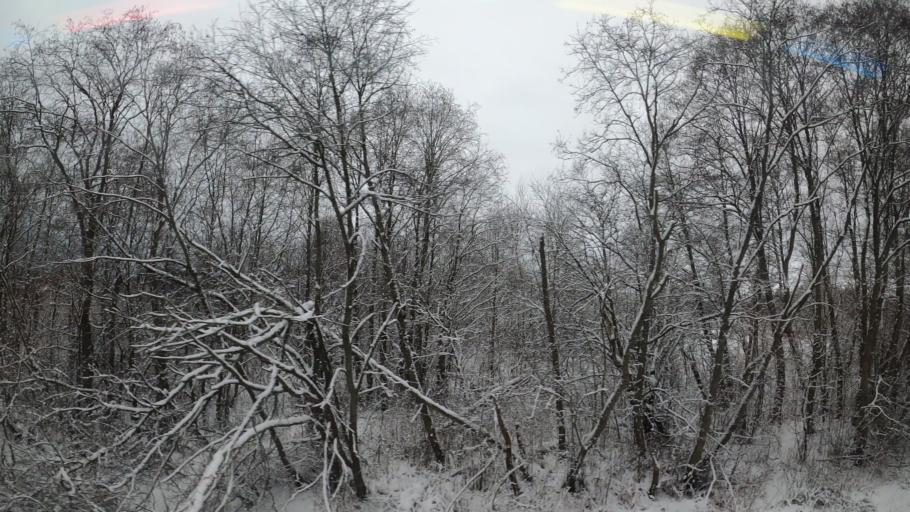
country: RU
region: Jaroslavl
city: Pereslavl'-Zalesskiy
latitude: 56.7195
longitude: 38.9076
